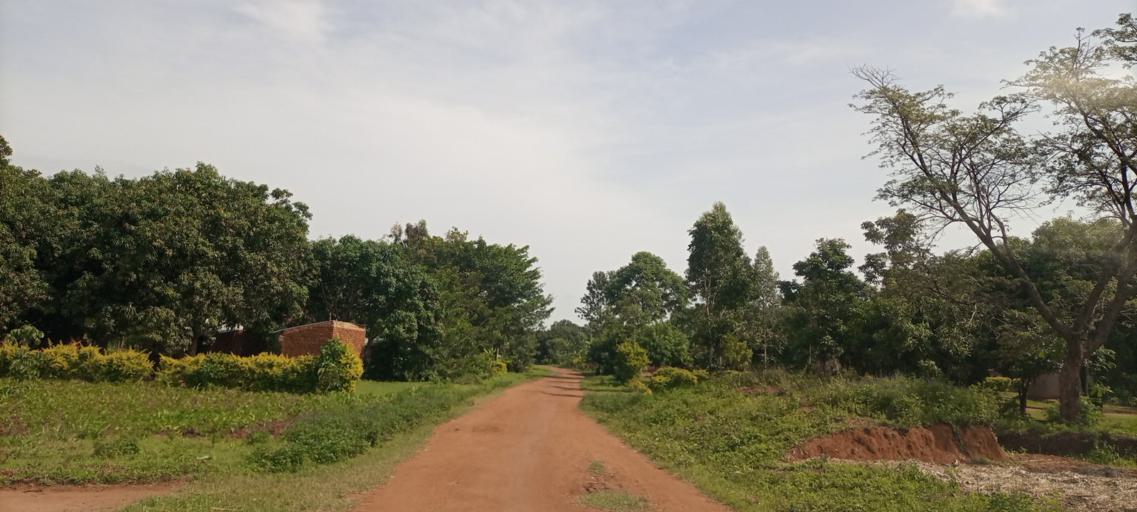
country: UG
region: Eastern Region
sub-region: Mbale District
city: Mbale
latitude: 1.1294
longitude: 34.0243
